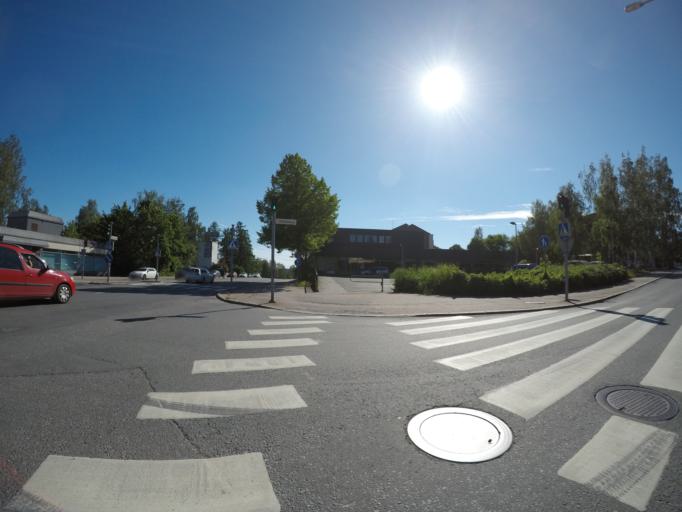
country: FI
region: Haeme
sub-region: Haemeenlinna
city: Haemeenlinna
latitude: 61.0035
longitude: 24.4890
